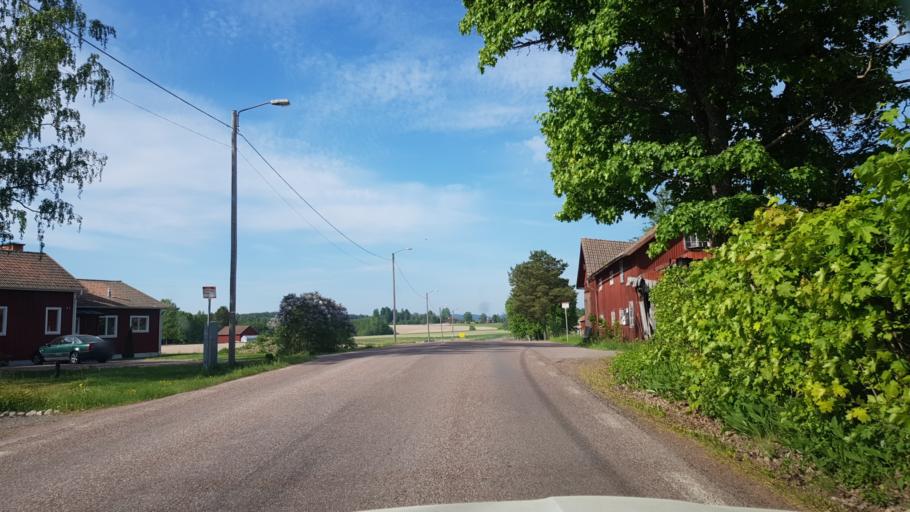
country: SE
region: Dalarna
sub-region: Saters Kommun
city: Saeter
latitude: 60.4168
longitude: 15.7318
